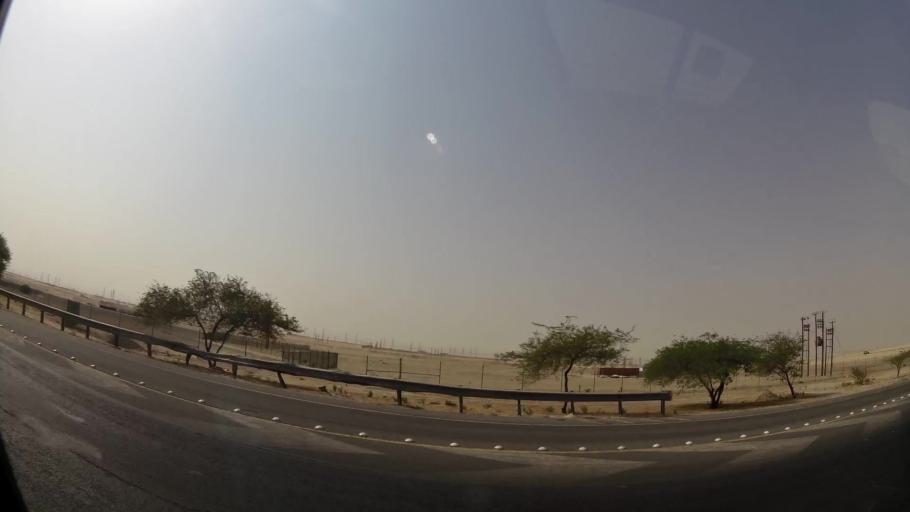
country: KW
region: Muhafazat al Jahra'
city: Al Jahra'
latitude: 29.3228
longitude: 47.6397
